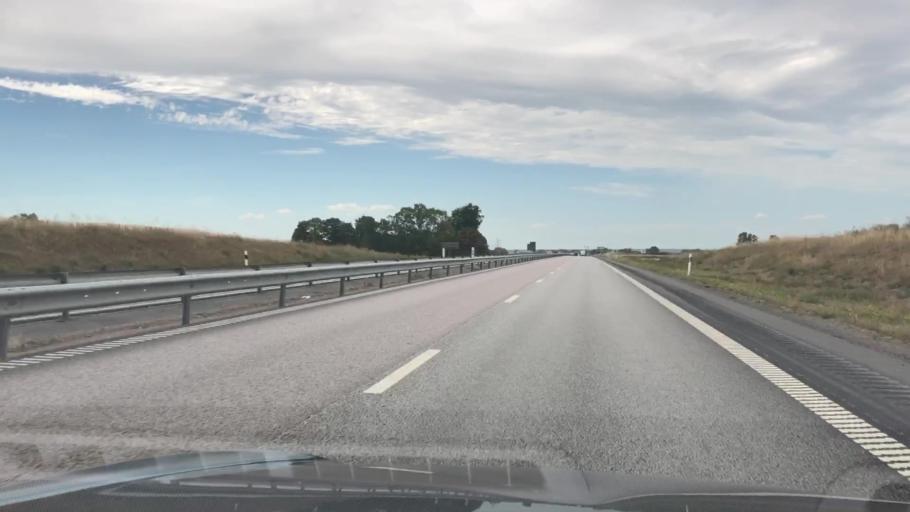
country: SE
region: Skane
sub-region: Kristianstads Kommun
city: Fjalkinge
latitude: 56.0326
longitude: 14.2475
